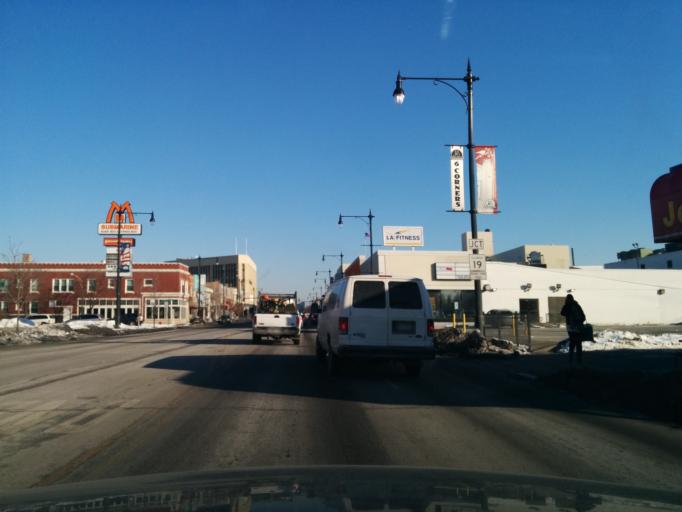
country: US
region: Illinois
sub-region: Cook County
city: Lincolnwood
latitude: 41.9517
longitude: -87.7472
